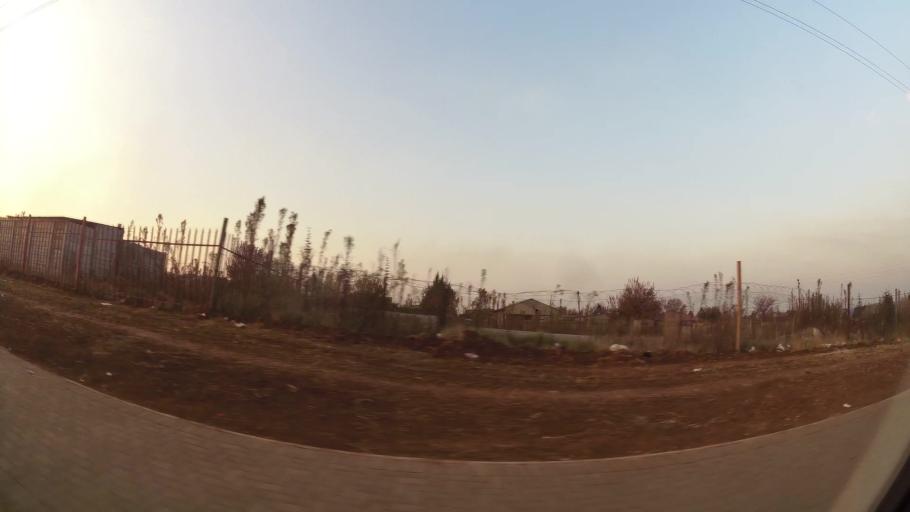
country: ZA
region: Gauteng
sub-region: Ekurhuleni Metropolitan Municipality
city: Springs
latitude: -26.2668
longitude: 28.3934
